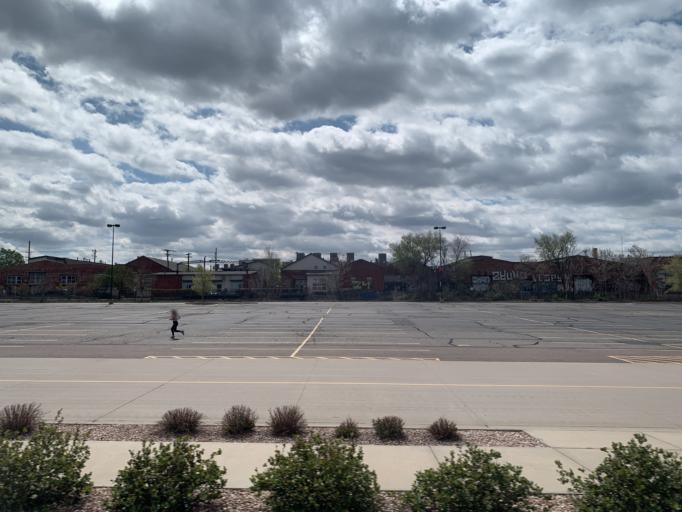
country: US
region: Colorado
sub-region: Denver County
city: Denver
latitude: 39.7648
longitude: -104.9834
